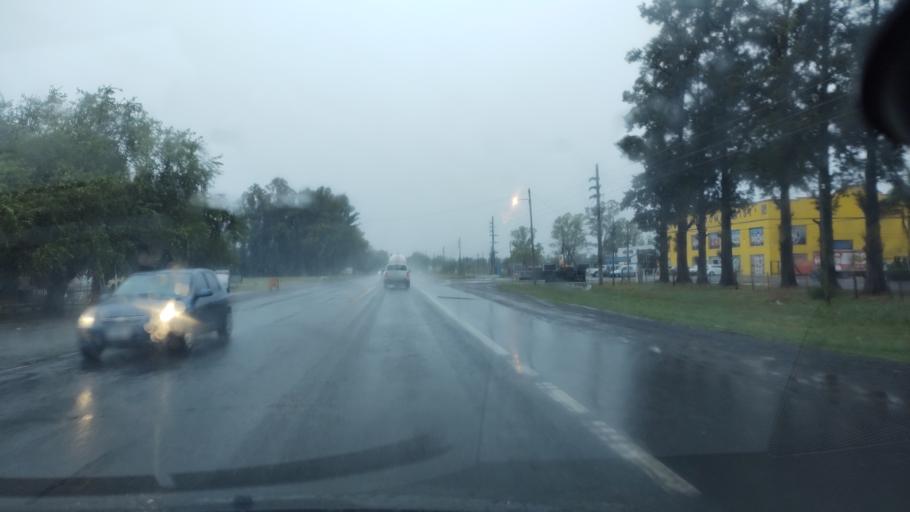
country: AR
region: Buenos Aires
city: Canuelas
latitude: -35.0376
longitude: -58.7581
